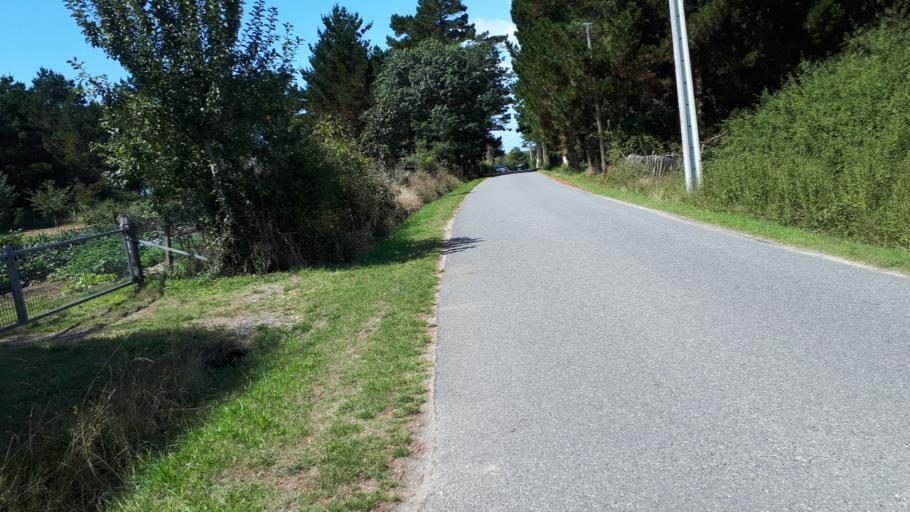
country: FR
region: Brittany
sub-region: Departement du Morbihan
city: Penestin
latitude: 47.4938
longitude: -2.4924
